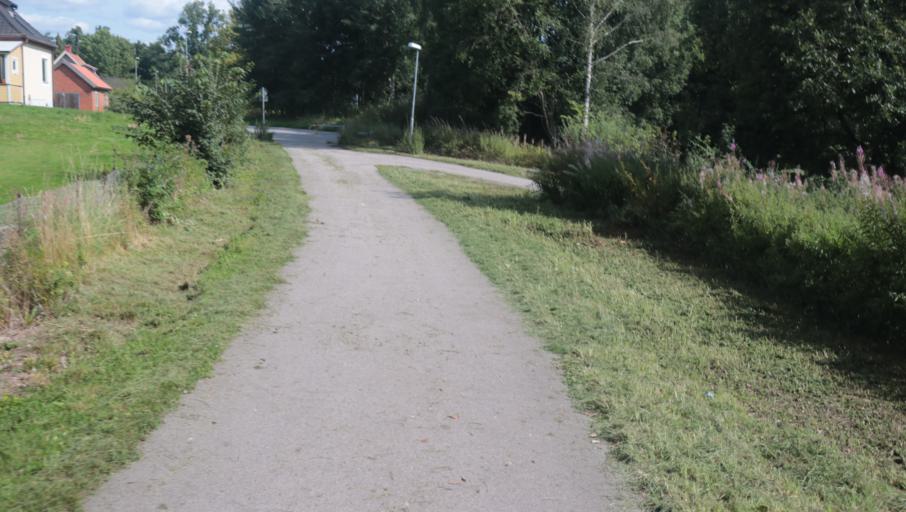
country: SE
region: Blekinge
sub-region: Karlshamns Kommun
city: Karlshamn
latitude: 56.2016
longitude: 14.8355
